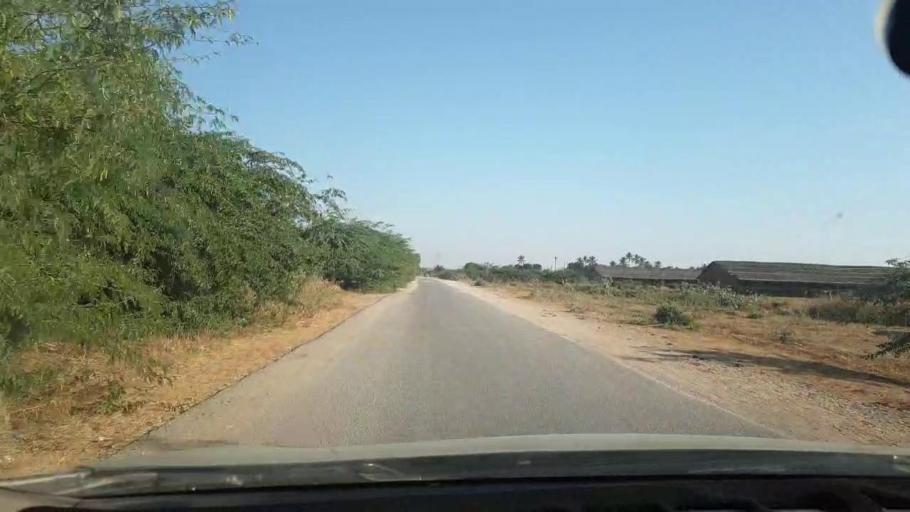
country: PK
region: Sindh
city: Malir Cantonment
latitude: 25.1711
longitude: 67.2011
